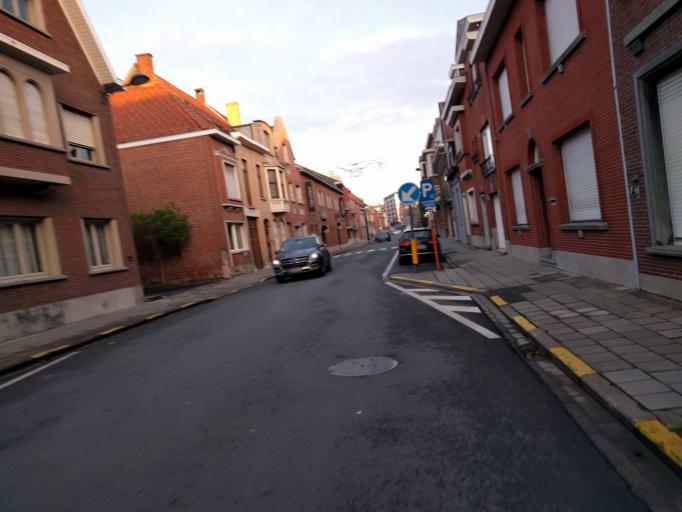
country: BE
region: Flanders
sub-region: Provincie West-Vlaanderen
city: Wevelgem
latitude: 50.8059
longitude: 3.1868
